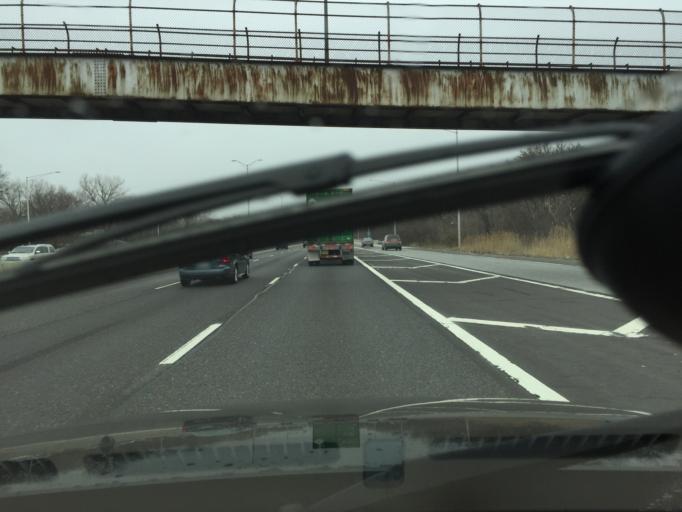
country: US
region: Illinois
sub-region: Cook County
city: Markham
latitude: 41.6046
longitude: -87.7050
